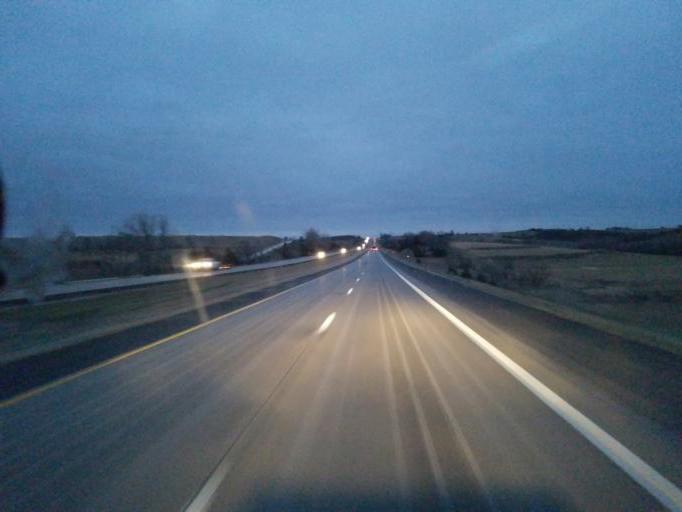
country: US
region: Iowa
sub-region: Cass County
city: Atlantic
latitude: 41.4971
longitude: -94.9118
